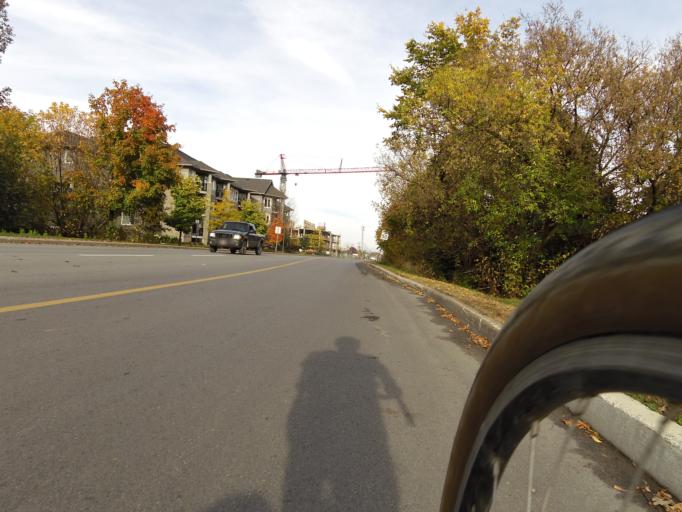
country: CA
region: Ontario
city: Carleton Place
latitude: 45.1370
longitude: -76.1322
